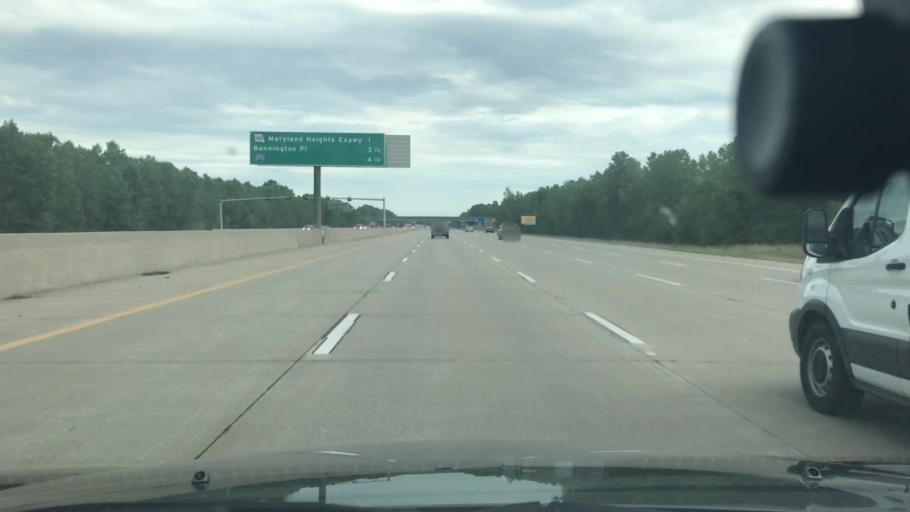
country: US
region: Missouri
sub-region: Saint Charles County
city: Saint Charles
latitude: 38.7242
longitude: -90.5133
